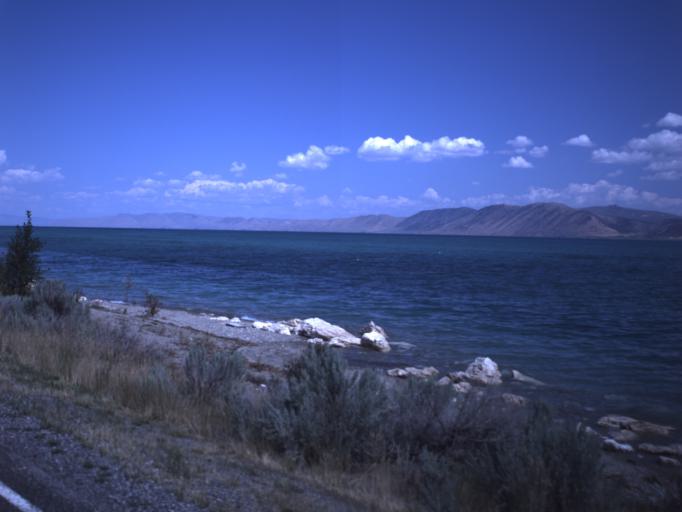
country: US
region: Utah
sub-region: Rich County
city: Randolph
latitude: 41.8689
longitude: -111.3652
